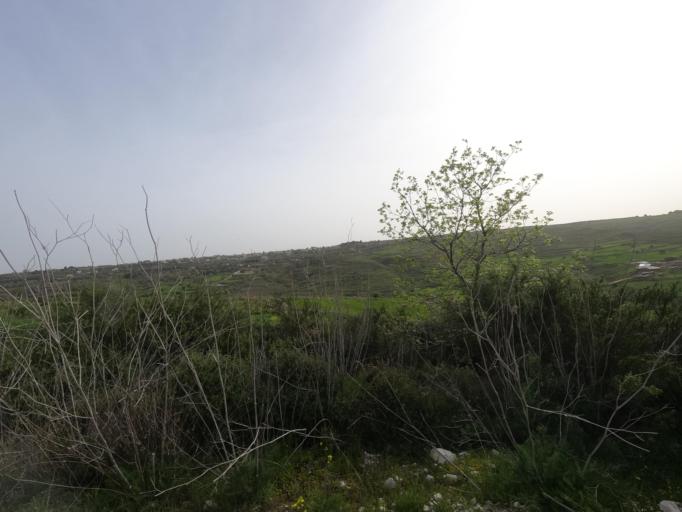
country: CY
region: Pafos
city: Pegeia
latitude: 34.9462
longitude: 32.3831
